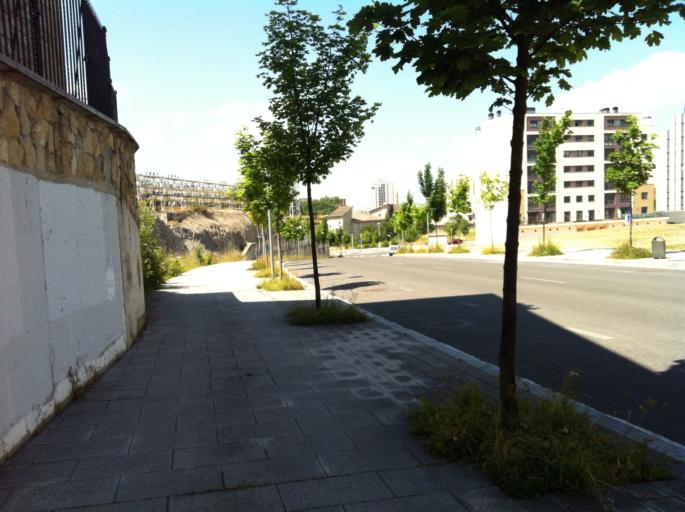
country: ES
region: Basque Country
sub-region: Provincia de Alava
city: Gasteiz / Vitoria
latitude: 42.8470
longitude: -2.6561
